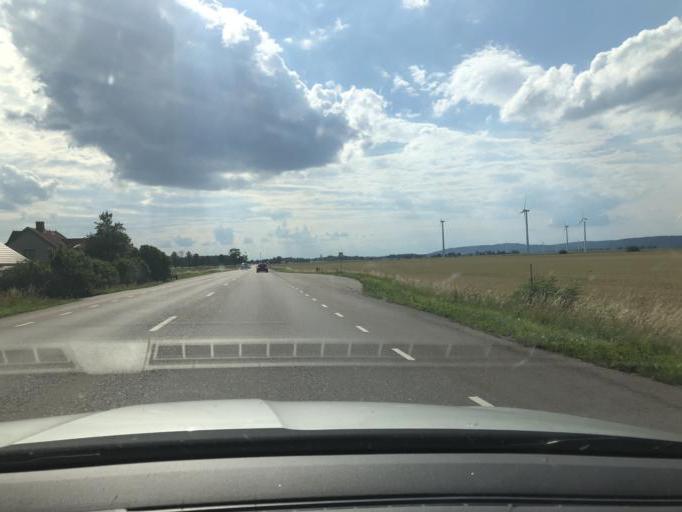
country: SE
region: OEstergoetland
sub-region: Vadstena Kommun
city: Herrestad
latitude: 58.3016
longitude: 14.8198
